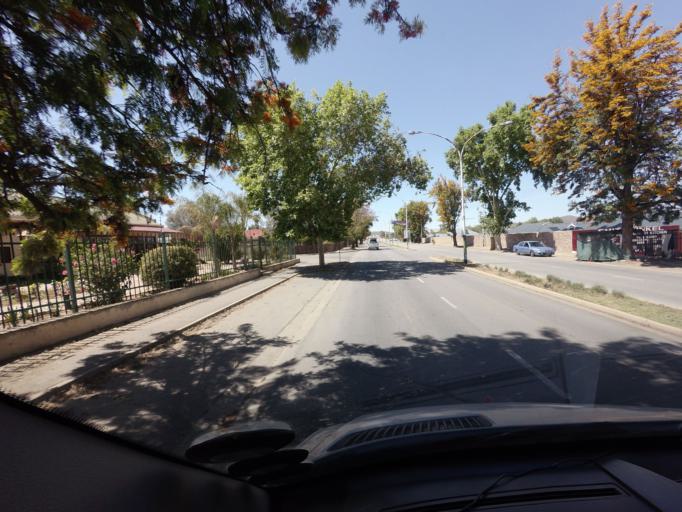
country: ZA
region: Western Cape
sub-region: Eden District Municipality
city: Oudtshoorn
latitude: -33.6073
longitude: 22.2116
